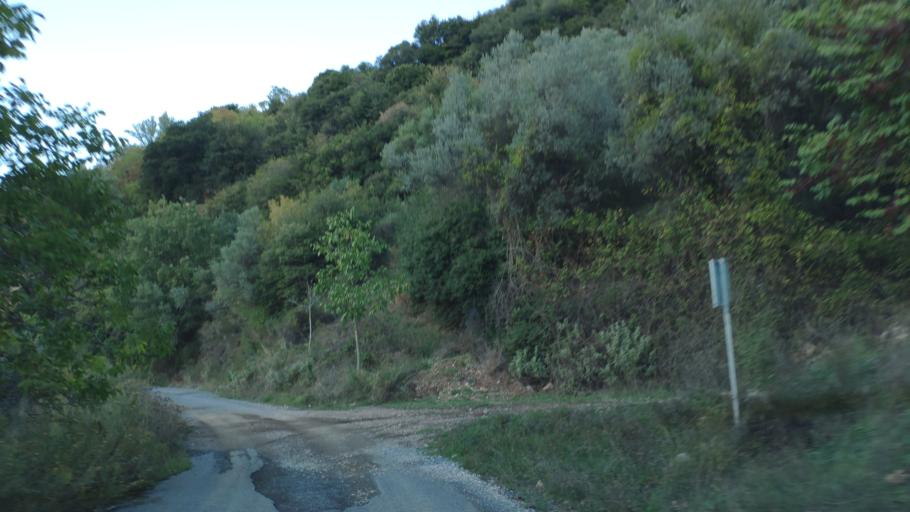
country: GR
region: Peloponnese
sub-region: Nomos Arkadias
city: Dimitsana
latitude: 37.5797
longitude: 22.0465
